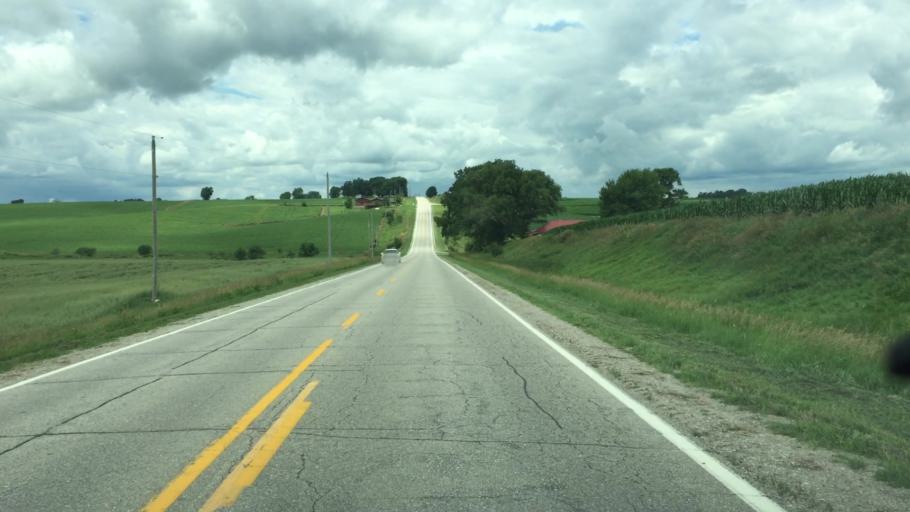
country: US
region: Iowa
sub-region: Jasper County
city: Monroe
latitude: 41.5736
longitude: -93.0757
